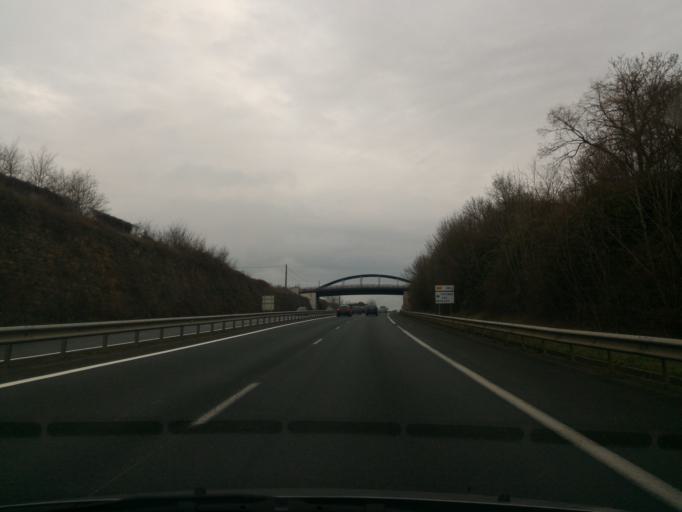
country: FR
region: Poitou-Charentes
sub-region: Departement de la Vienne
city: Vivonne
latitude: 46.4287
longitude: 0.2588
